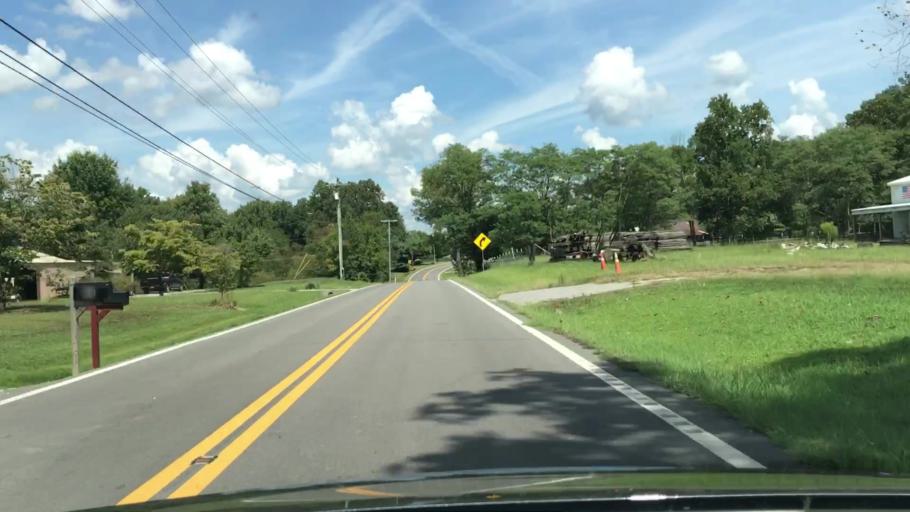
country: US
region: Tennessee
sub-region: Sumner County
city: Portland
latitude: 36.5410
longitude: -86.5229
